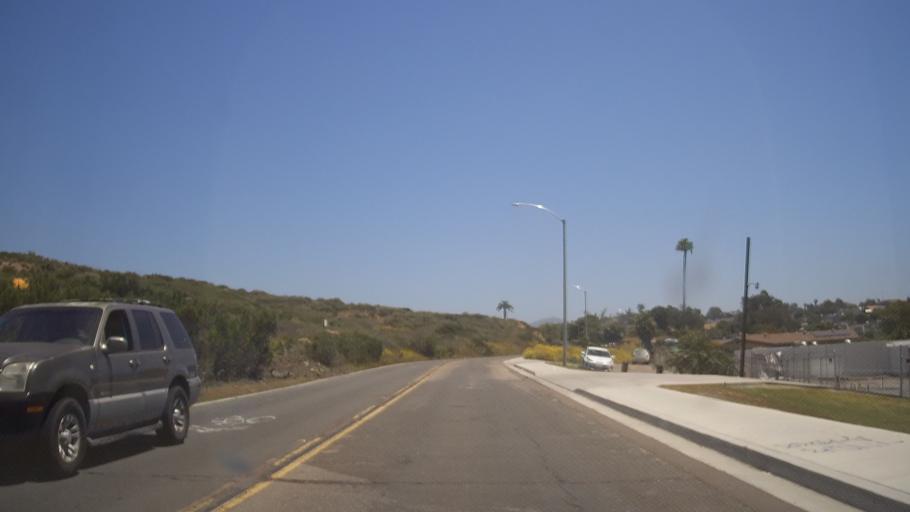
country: US
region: California
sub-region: San Diego County
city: National City
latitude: 32.7104
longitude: -117.0774
